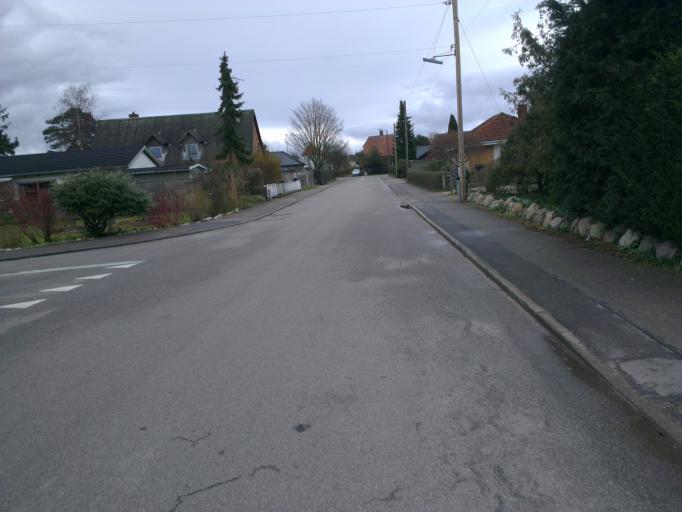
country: DK
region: Capital Region
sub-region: Frederikssund Kommune
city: Frederikssund
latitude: 55.8262
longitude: 12.0706
